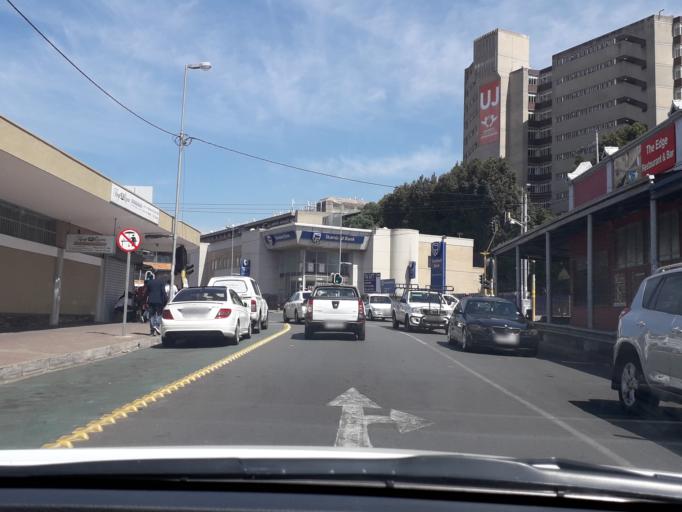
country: ZA
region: Gauteng
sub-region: City of Johannesburg Metropolitan Municipality
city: Johannesburg
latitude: -26.1946
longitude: 28.0582
